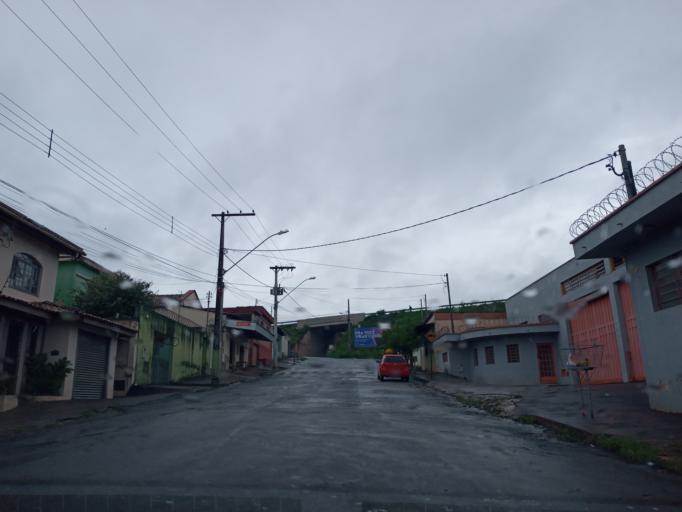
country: BR
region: Minas Gerais
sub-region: Pitangui
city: Pitangui
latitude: -19.8708
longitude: -44.9842
